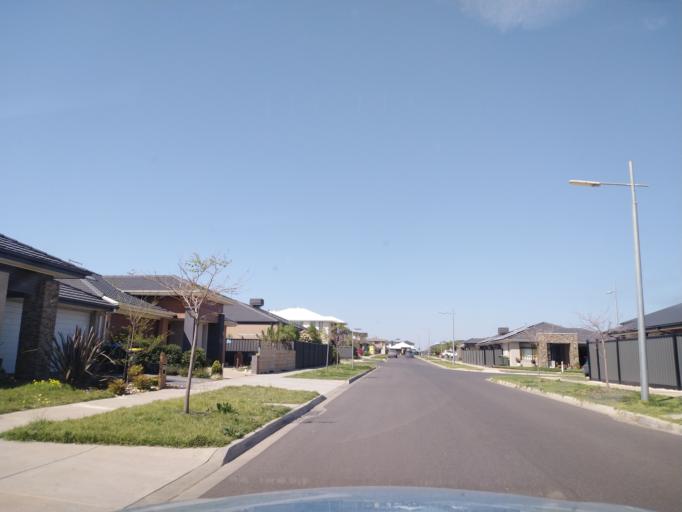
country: AU
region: Victoria
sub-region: Wyndham
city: Williams Landing
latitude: -37.8404
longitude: 144.7406
